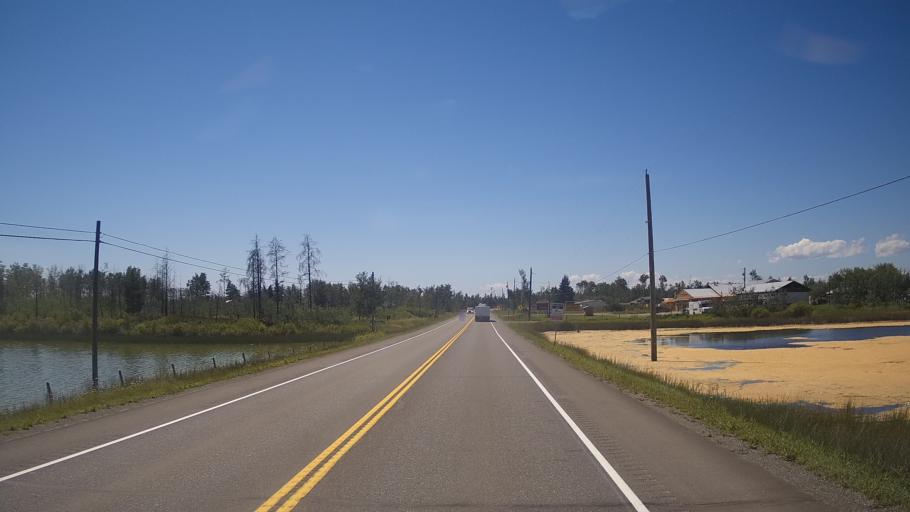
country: CA
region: British Columbia
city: Cache Creek
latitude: 51.3195
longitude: -121.3885
